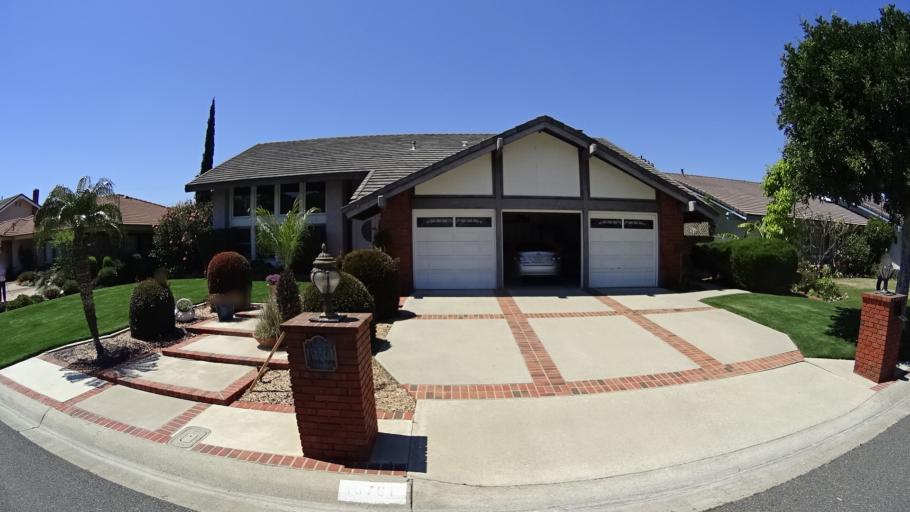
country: US
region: California
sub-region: Orange County
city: Villa Park
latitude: 33.8058
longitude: -117.8176
